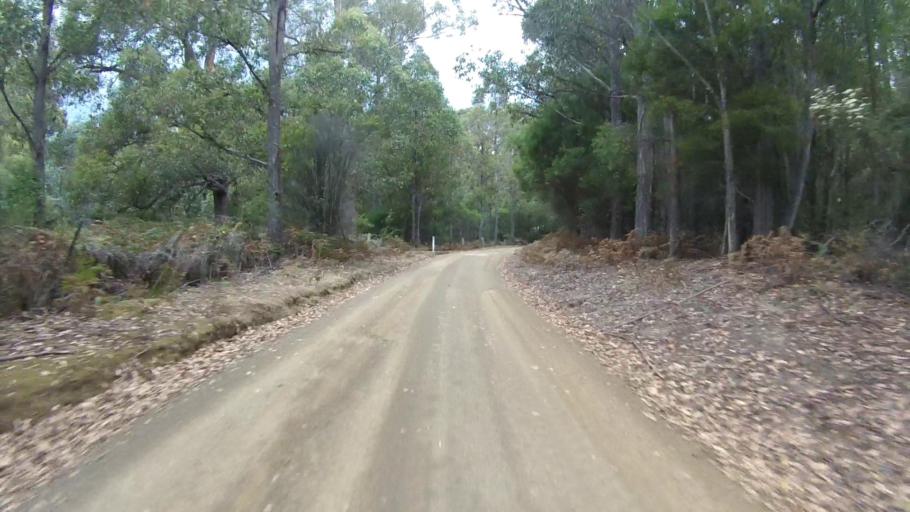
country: AU
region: Tasmania
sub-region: Huon Valley
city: Huonville
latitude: -42.9590
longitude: 147.0510
